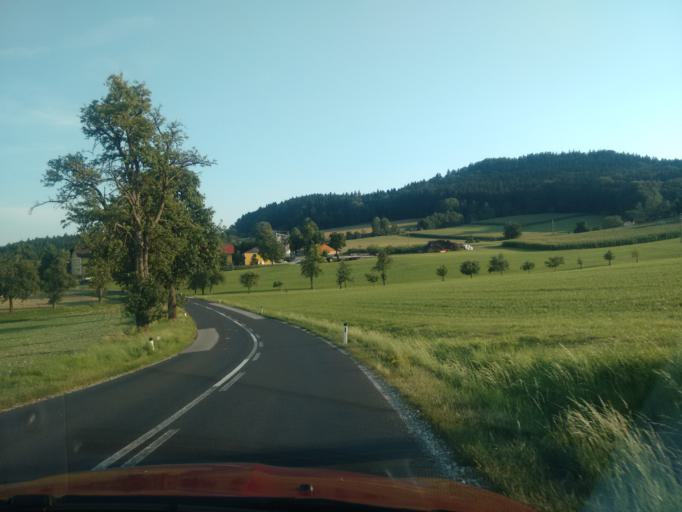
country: AT
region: Upper Austria
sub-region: Politischer Bezirk Vocklabruck
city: Wolfsegg am Hausruck
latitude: 48.1498
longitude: 13.6807
